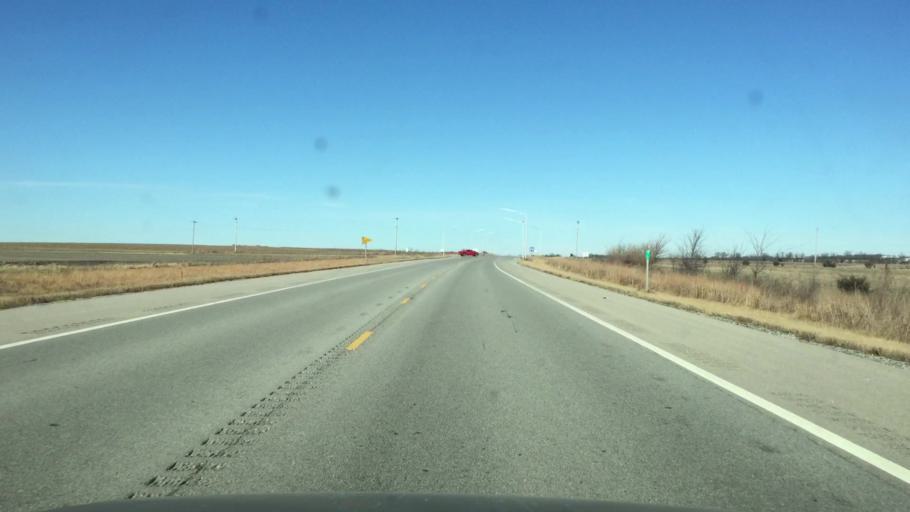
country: US
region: Kansas
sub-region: Allen County
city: Iola
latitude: 37.9490
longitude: -95.3809
